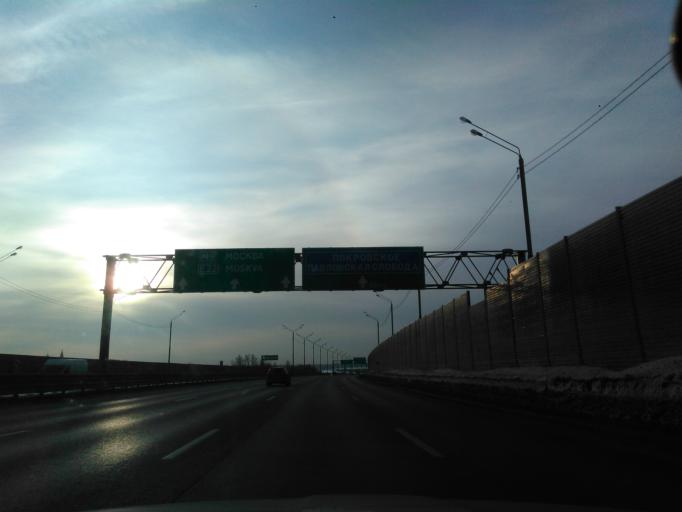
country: RU
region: Moskovskaya
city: Rozhdestveno
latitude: 55.8154
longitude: 37.0226
